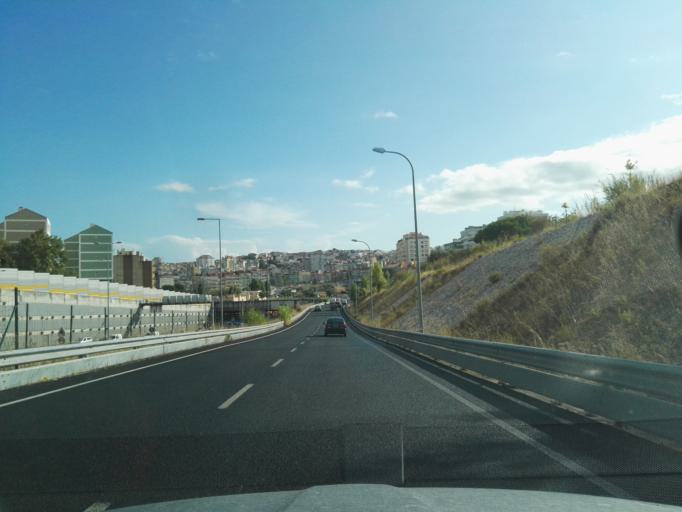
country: PT
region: Lisbon
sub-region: Odivelas
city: Pontinha
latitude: 38.7556
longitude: -9.2082
